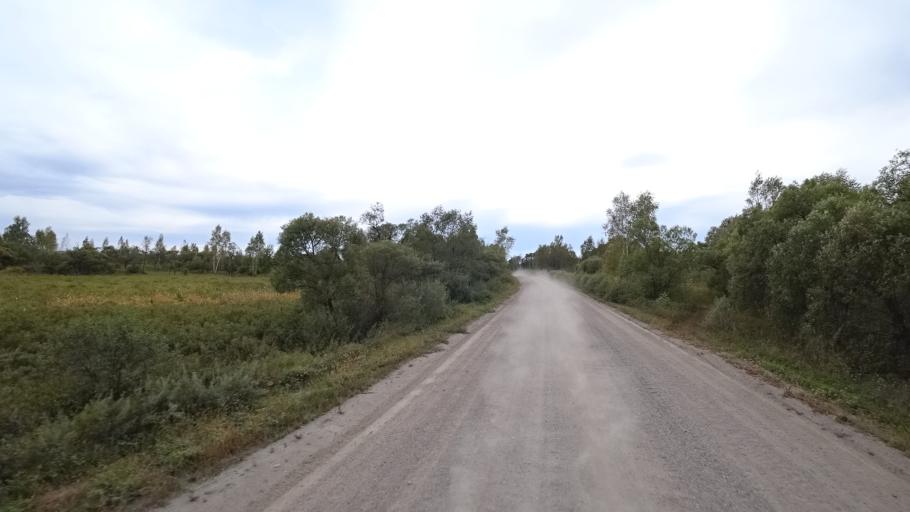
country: RU
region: Amur
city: Arkhara
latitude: 49.3835
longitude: 130.2211
